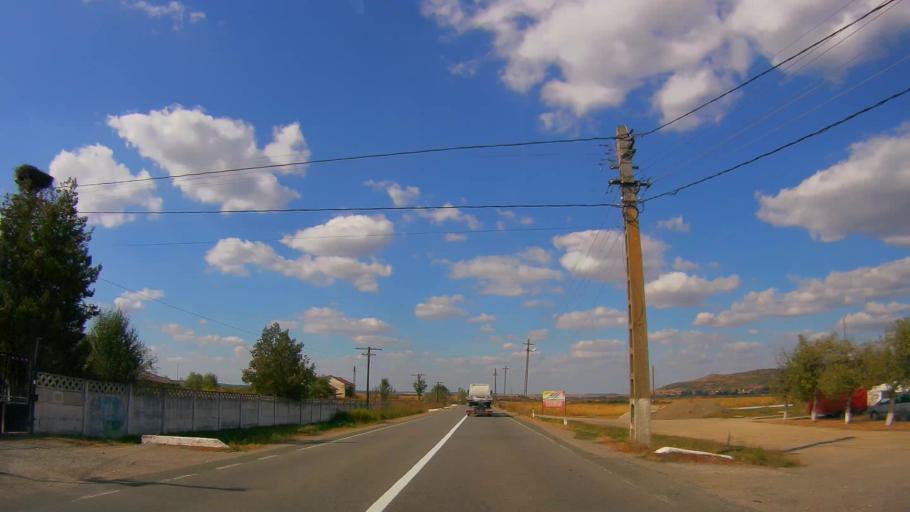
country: RO
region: Salaj
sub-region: Comuna Bobota
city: Dersida
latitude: 47.3651
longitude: 22.7922
